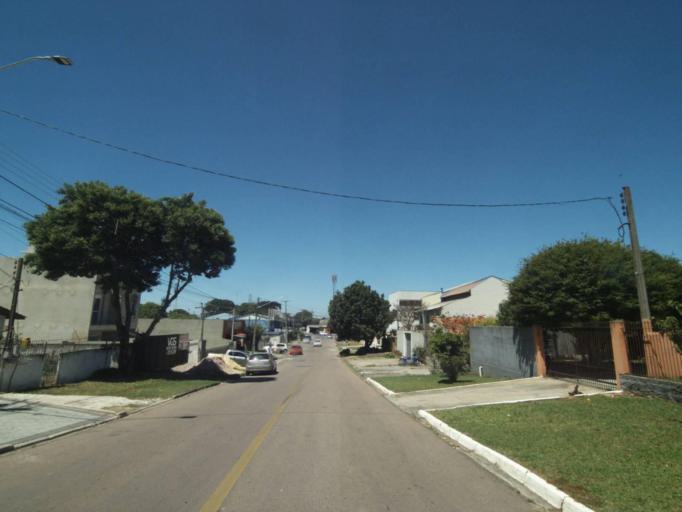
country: BR
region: Parana
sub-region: Curitiba
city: Curitiba
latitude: -25.4820
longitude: -49.3457
